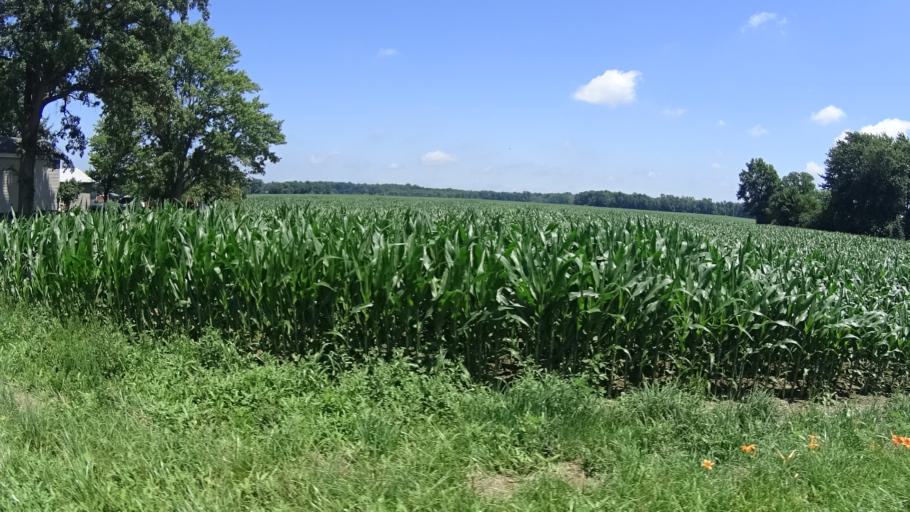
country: US
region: Ohio
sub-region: Huron County
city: Wakeman
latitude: 41.3431
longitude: -82.4239
